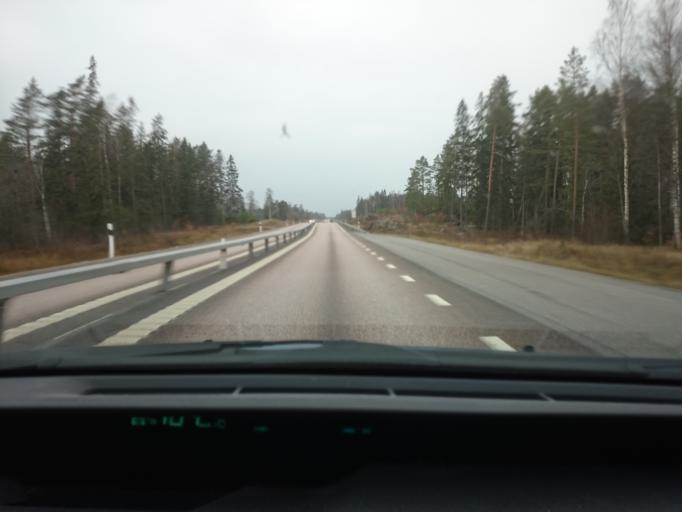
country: SE
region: Vaestmanland
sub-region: Sala Kommun
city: Sala
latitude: 59.9949
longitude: 16.4356
